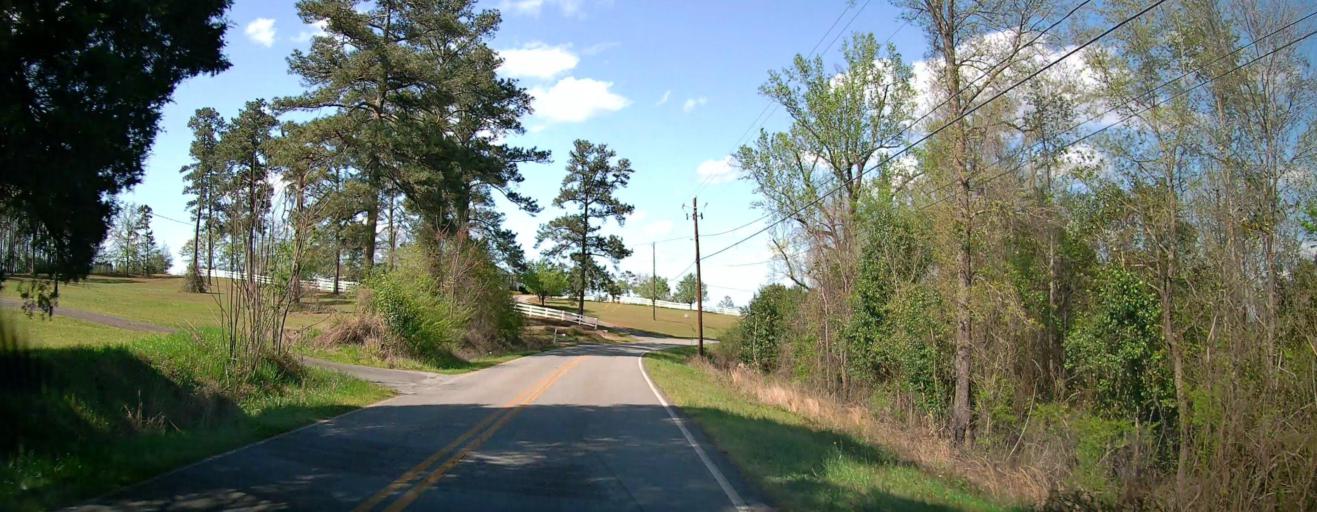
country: US
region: Georgia
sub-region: Bibb County
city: Macon
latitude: 32.8051
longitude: -83.4858
